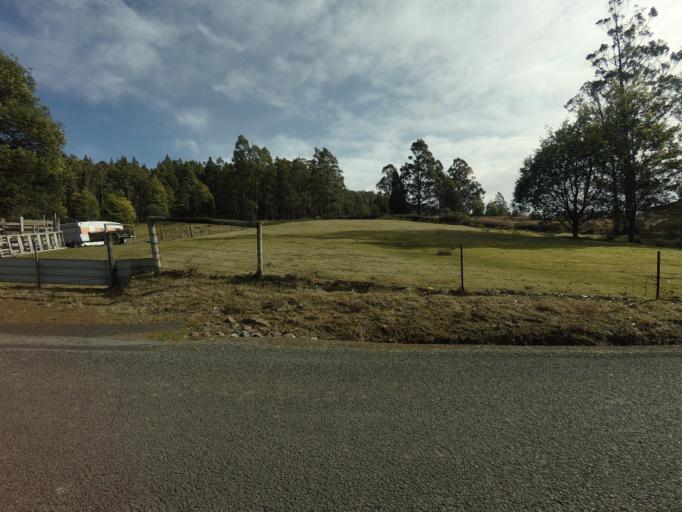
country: AU
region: Tasmania
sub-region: Kingborough
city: Margate
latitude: -43.0127
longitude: 147.1603
